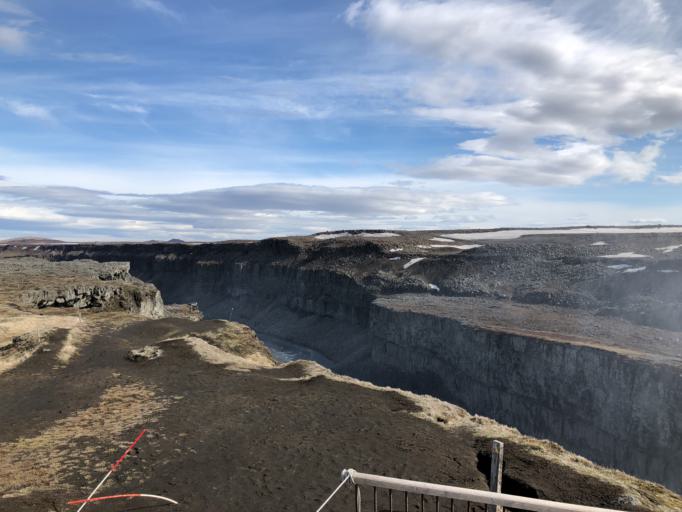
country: IS
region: Northeast
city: Husavik
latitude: 65.8161
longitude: -16.3873
